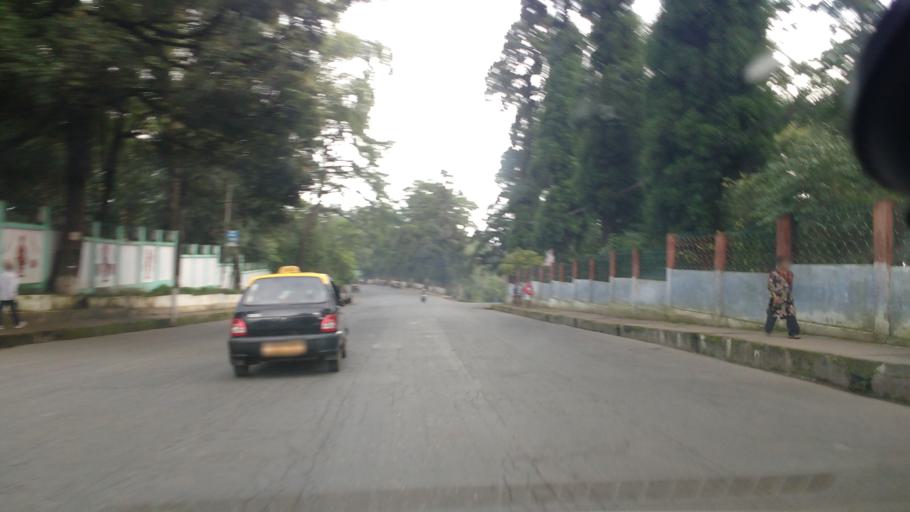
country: IN
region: Meghalaya
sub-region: East Khasi Hills
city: Shillong
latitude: 25.5699
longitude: 91.8782
